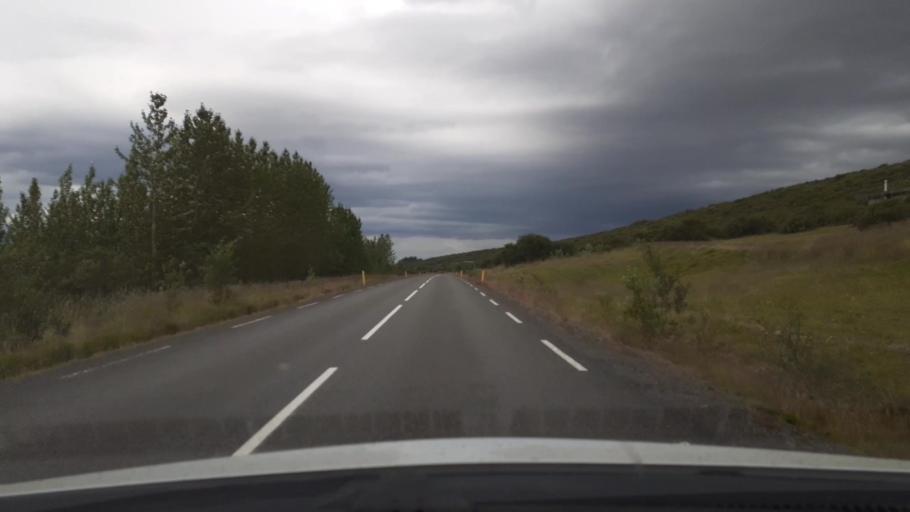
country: IS
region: West
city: Borgarnes
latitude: 64.5420
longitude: -21.5532
